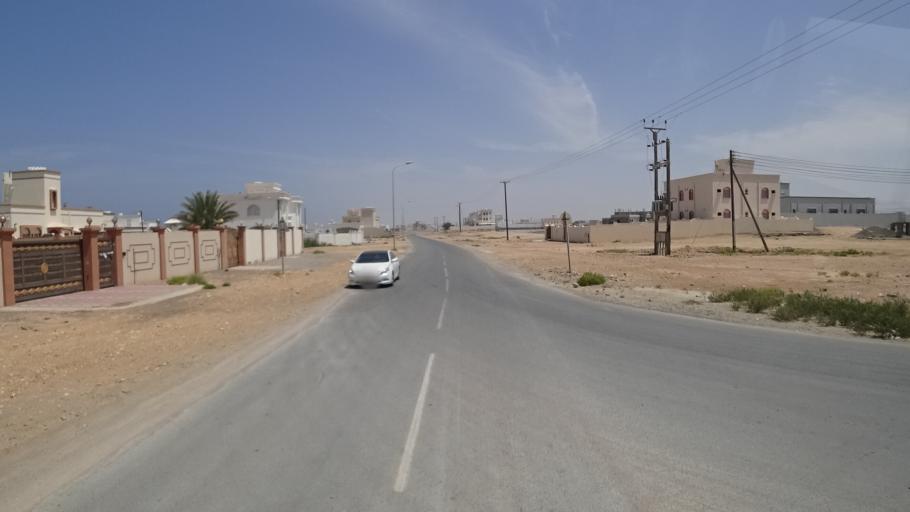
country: OM
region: Ash Sharqiyah
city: Sur
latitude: 22.6202
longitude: 59.4565
